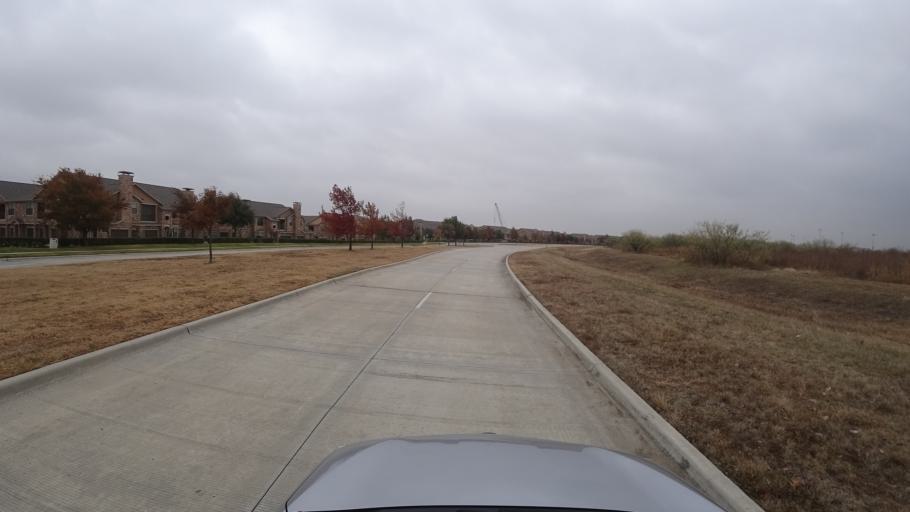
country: US
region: Texas
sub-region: Denton County
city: Lewisville
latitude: 33.0390
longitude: -96.9310
